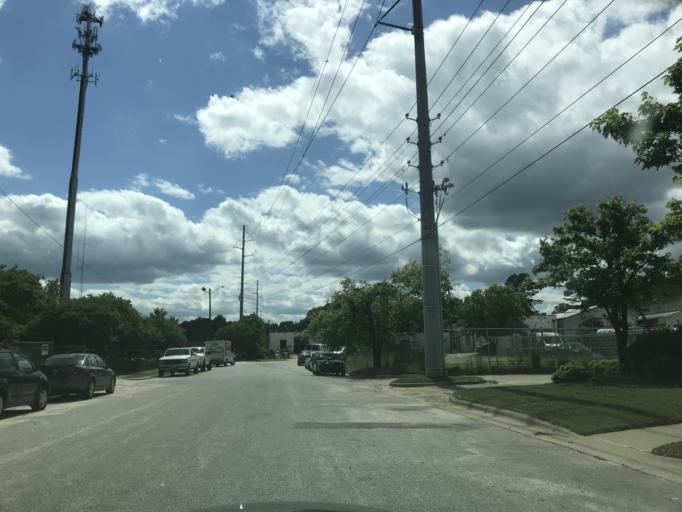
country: US
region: North Carolina
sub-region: Wake County
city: Raleigh
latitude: 35.8035
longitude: -78.6328
